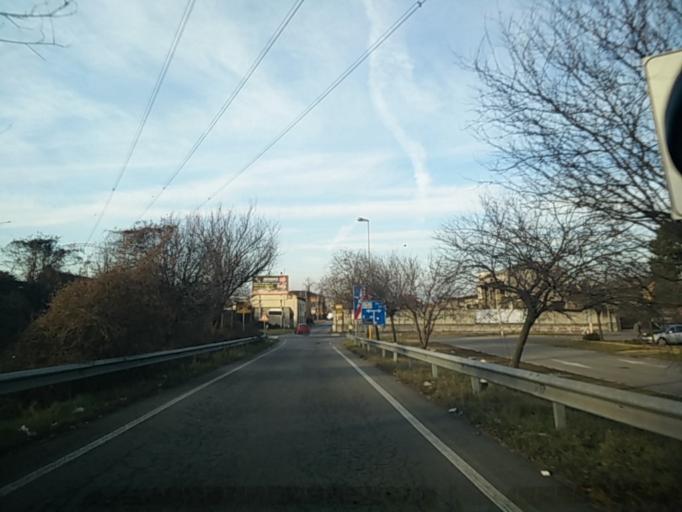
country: IT
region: Lombardy
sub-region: Provincia di Monza e Brianza
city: Cesano Maderno
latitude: 45.6287
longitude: 9.1635
